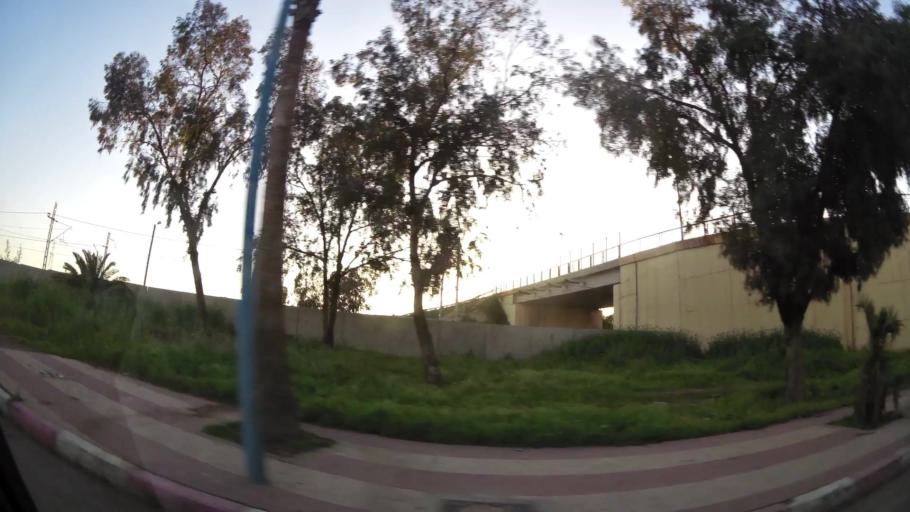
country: MA
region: Chaouia-Ouardigha
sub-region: Settat Province
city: Settat
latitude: 32.9899
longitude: -7.6207
